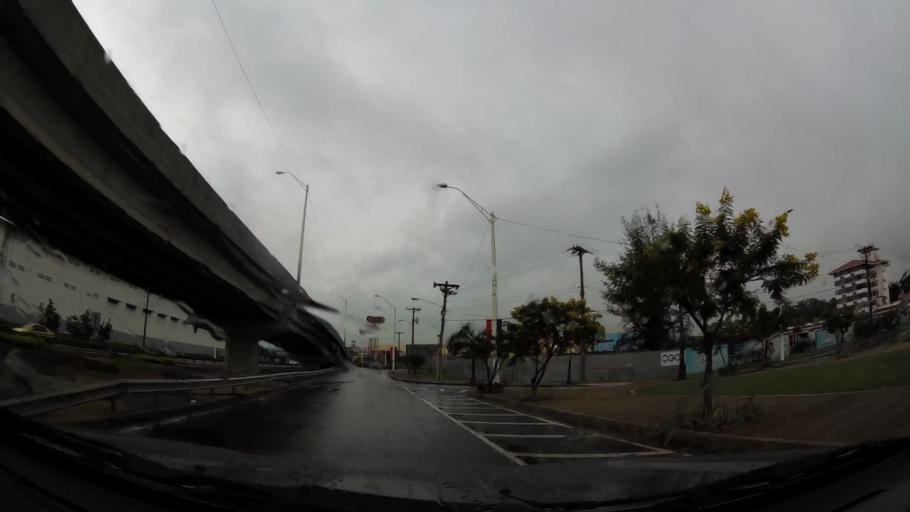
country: PA
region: Colon
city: Arco Iris
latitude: 9.3403
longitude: -79.8878
